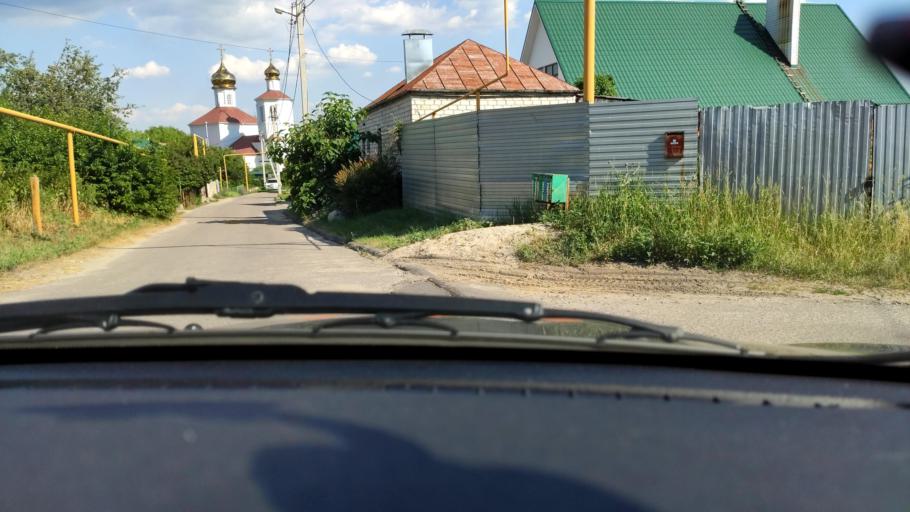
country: RU
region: Voronezj
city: Ramon'
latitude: 51.8214
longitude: 39.2762
